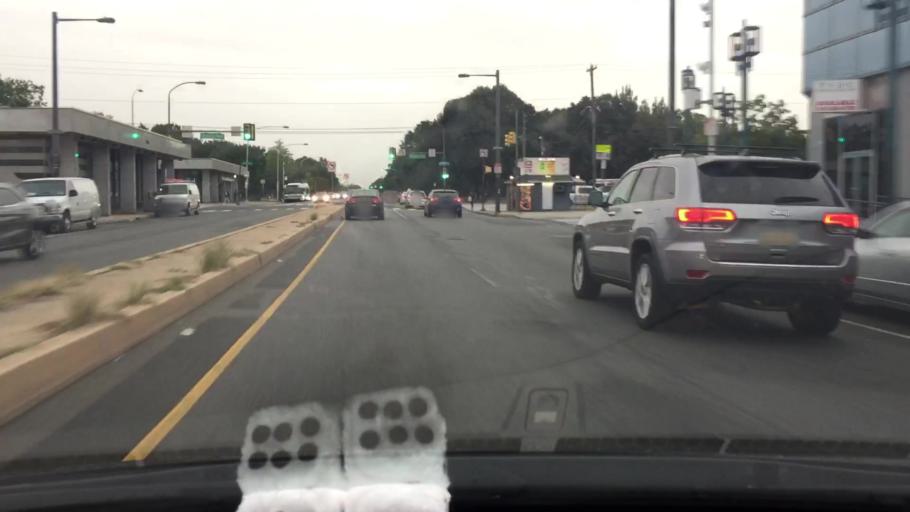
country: US
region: Pennsylvania
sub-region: Philadelphia County
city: Philadelphia
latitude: 39.9176
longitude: -75.1712
